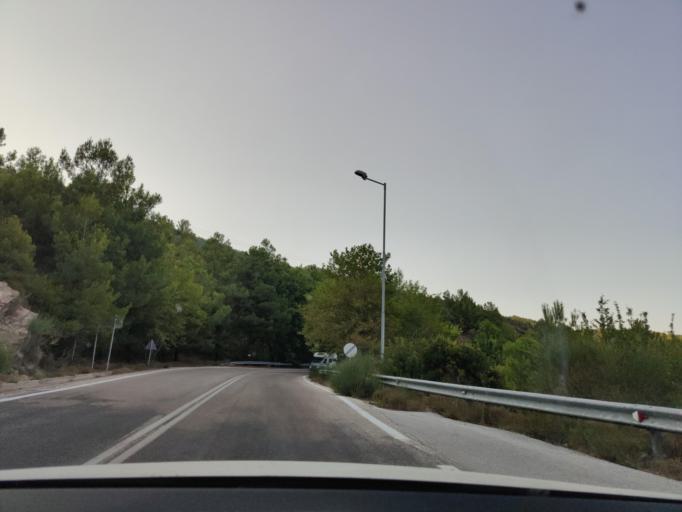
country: GR
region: East Macedonia and Thrace
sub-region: Nomos Kavalas
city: Potamia
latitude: 40.6184
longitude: 24.7585
